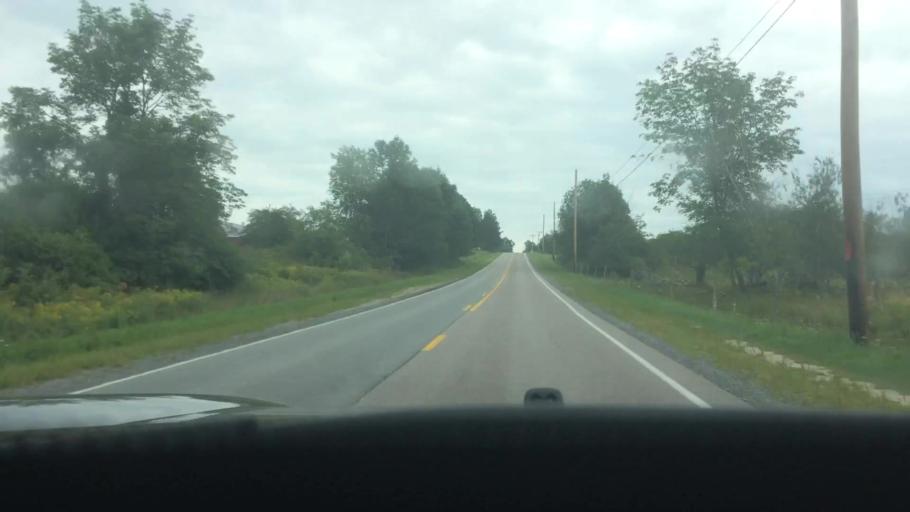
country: US
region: New York
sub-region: St. Lawrence County
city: Hannawa Falls
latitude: 44.5379
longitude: -75.0450
